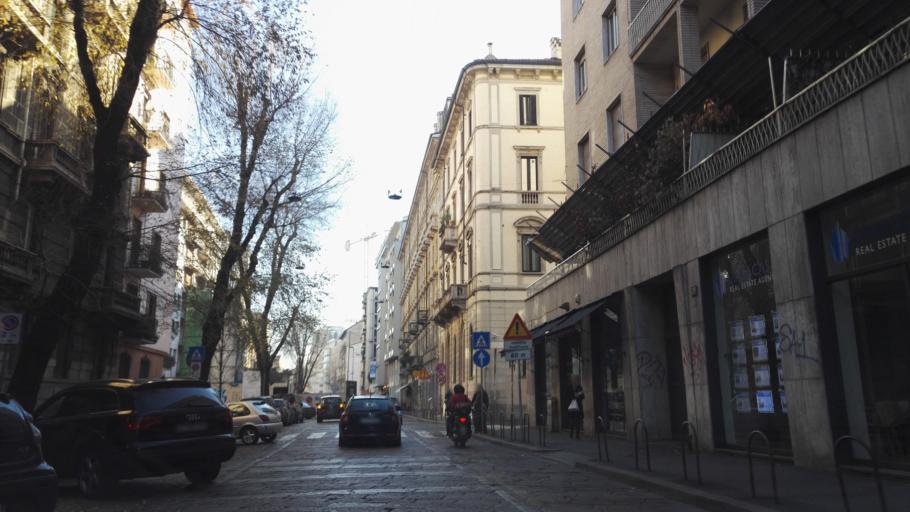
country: IT
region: Lombardy
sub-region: Citta metropolitana di Milano
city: Milano
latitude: 45.4606
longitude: 9.1748
